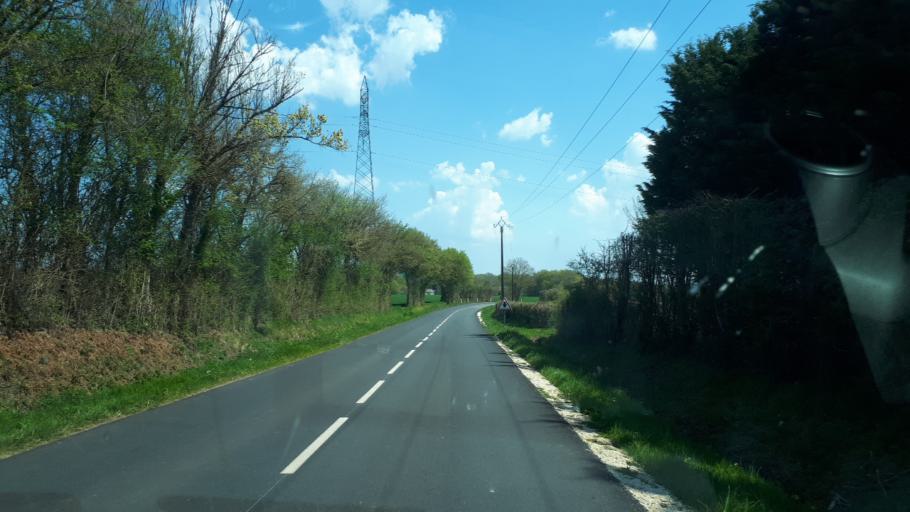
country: FR
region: Centre
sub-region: Departement du Cher
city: Sancerre
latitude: 47.3038
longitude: 2.6906
